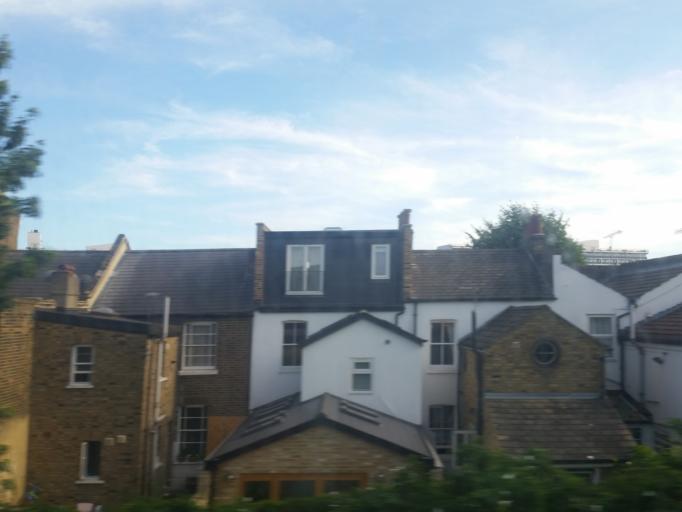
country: GB
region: England
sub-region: Greater London
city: Hackney
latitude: 51.5470
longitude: -0.0400
